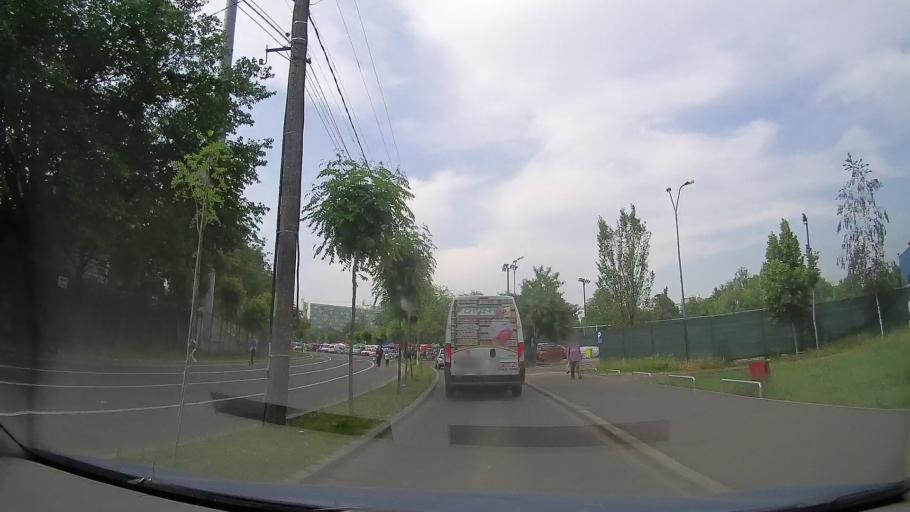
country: RO
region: Timis
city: Timisoara
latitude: 45.7413
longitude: 21.2426
